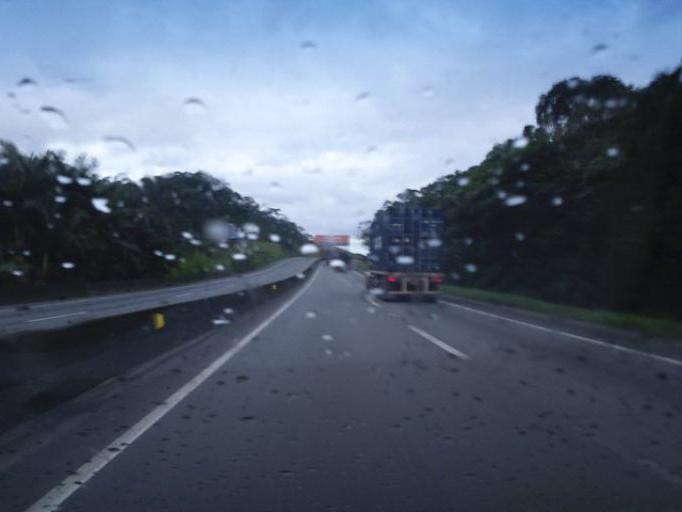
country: BR
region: Parana
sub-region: Guaratuba
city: Guaratuba
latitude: -25.9527
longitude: -48.9028
